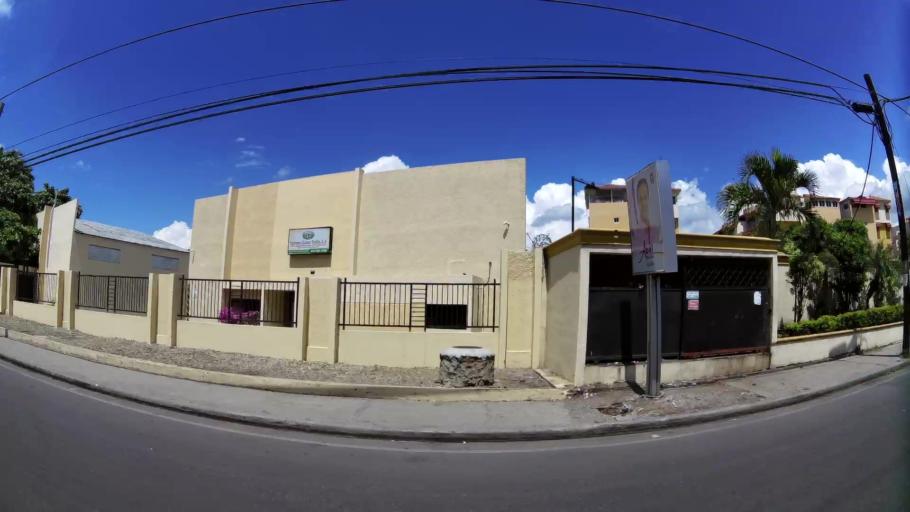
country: DO
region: Santiago
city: Santiago de los Caballeros
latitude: 19.4752
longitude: -70.6744
